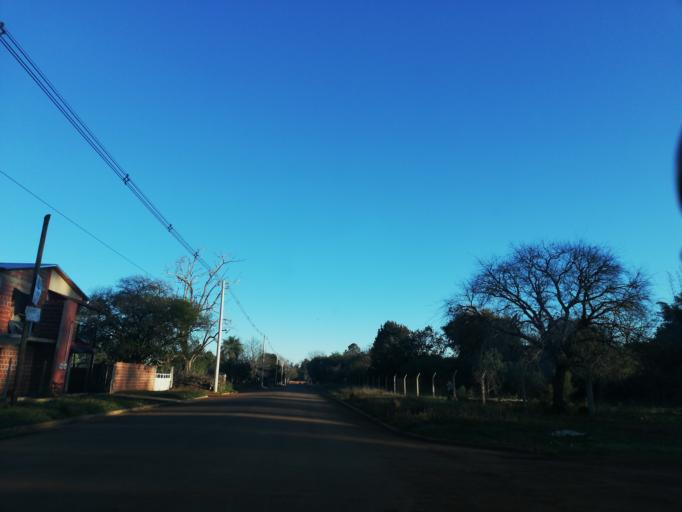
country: AR
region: Misiones
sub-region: Departamento de Candelaria
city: Candelaria
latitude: -27.4668
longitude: -55.7493
